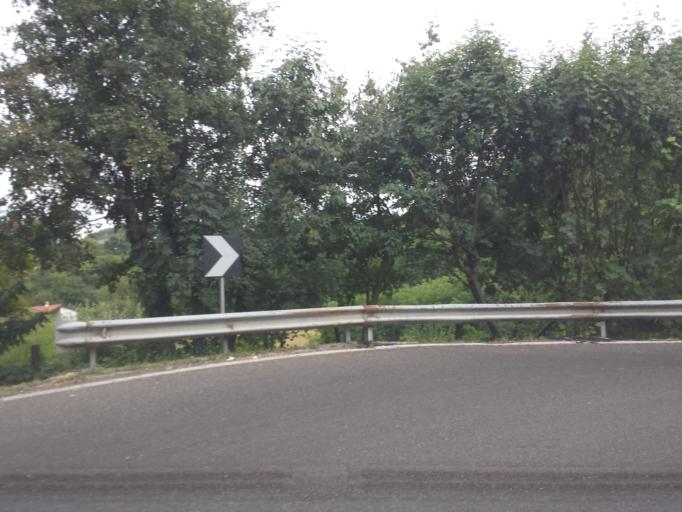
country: IT
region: Veneto
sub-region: Provincia di Vicenza
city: Castelgomberto
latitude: 45.5854
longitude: 11.4052
